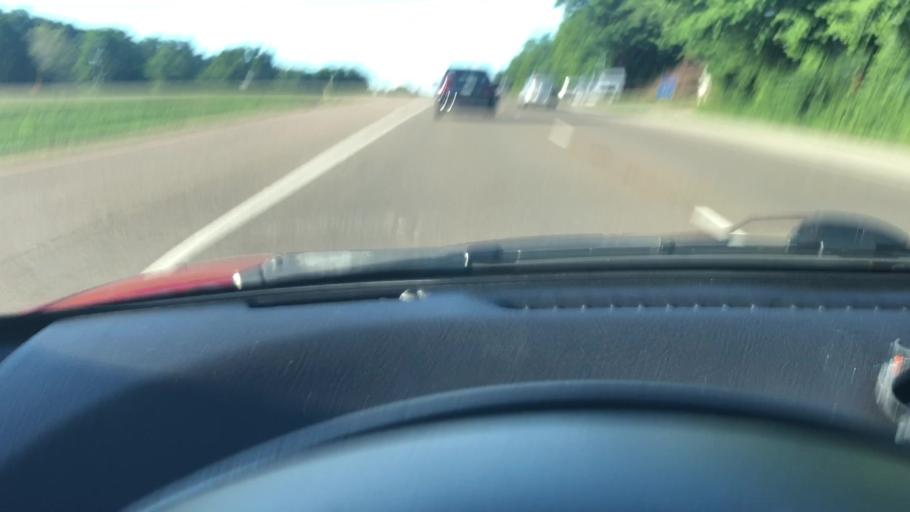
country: US
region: Tennessee
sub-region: Jefferson County
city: Jefferson City
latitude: 36.0674
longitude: -83.4790
